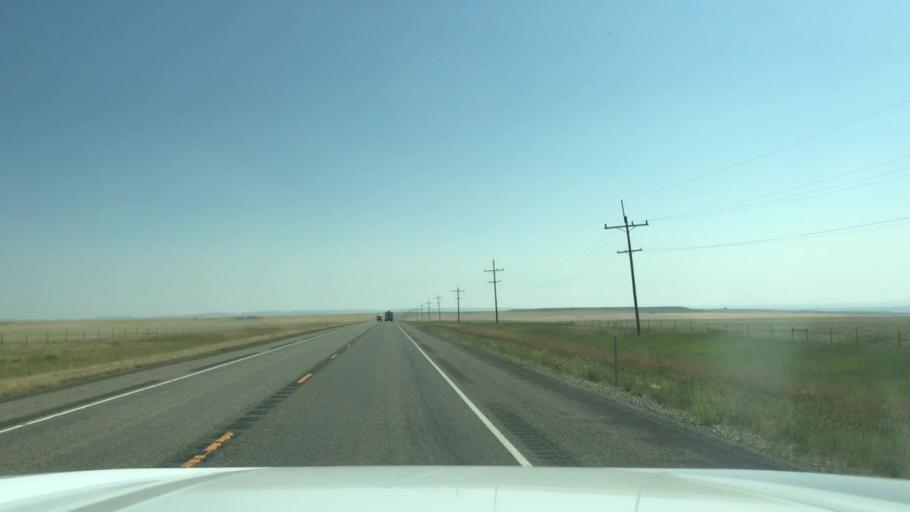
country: US
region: Montana
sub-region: Wheatland County
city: Harlowton
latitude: 46.5034
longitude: -109.7661
